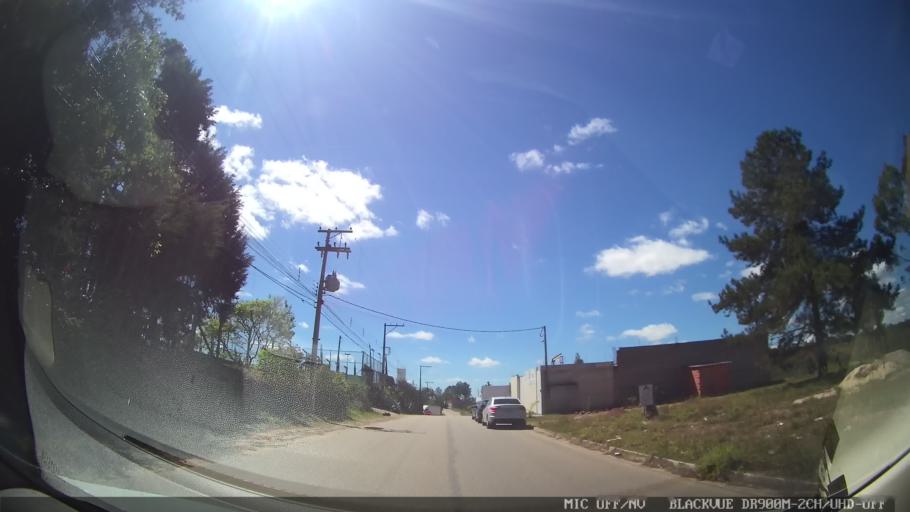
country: BR
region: Sao Paulo
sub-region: Campo Limpo Paulista
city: Campo Limpo Paulista
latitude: -23.1796
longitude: -46.7429
